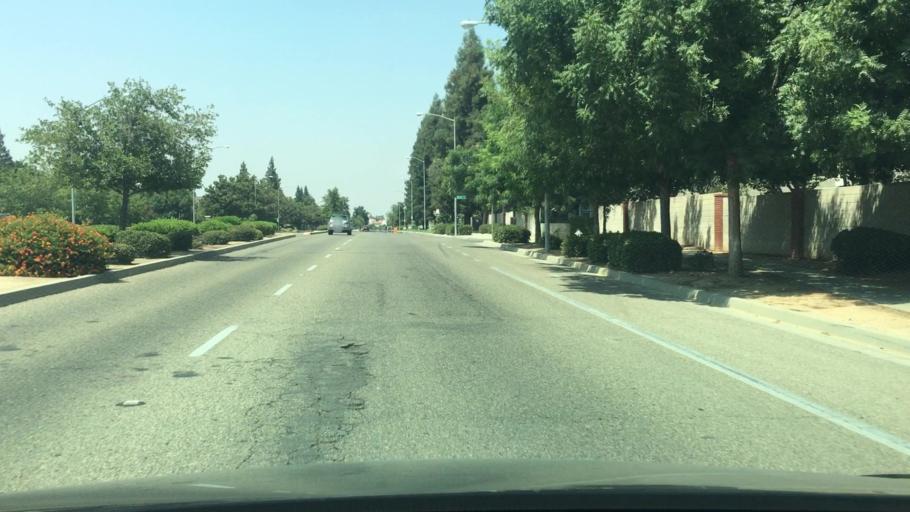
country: US
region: California
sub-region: Fresno County
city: Clovis
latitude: 36.8603
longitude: -119.7567
